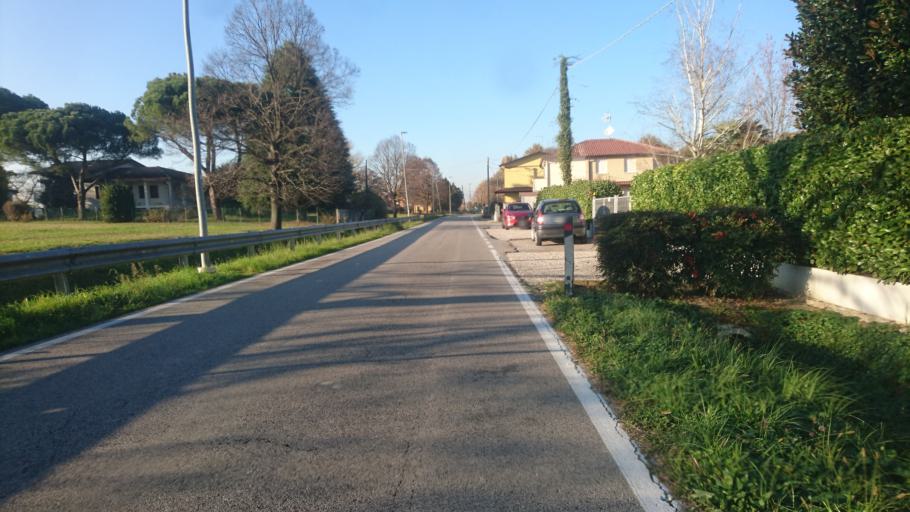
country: IT
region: Veneto
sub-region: Provincia di Padova
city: Villaguattera
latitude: 45.4471
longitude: 11.8139
